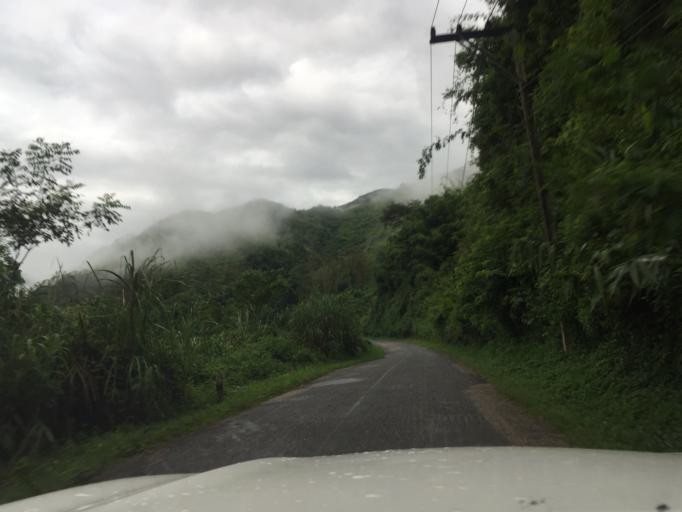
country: LA
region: Oudomxai
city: Muang La
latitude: 20.9378
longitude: 102.2077
